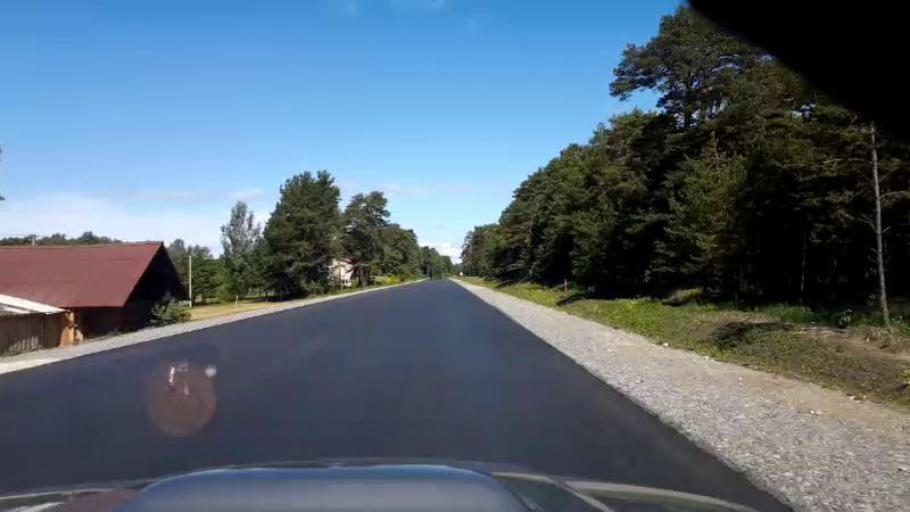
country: LV
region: Salacgrivas
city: Ainazi
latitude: 57.8125
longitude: 24.3474
